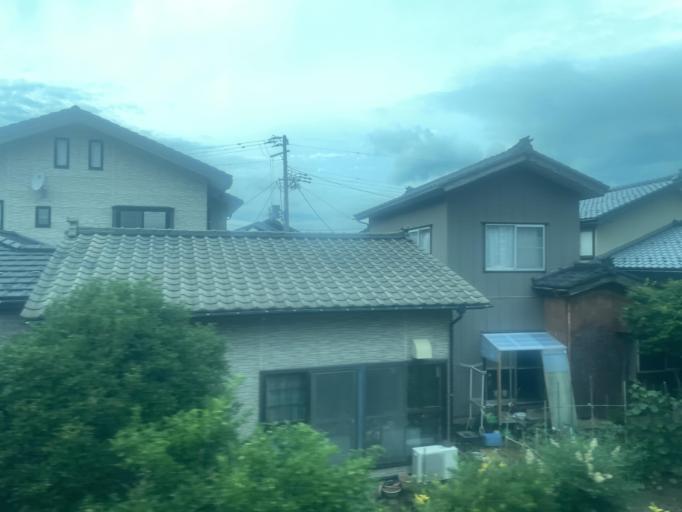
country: JP
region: Niigata
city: Yoshida-kasugacho
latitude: 37.6847
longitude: 138.8692
